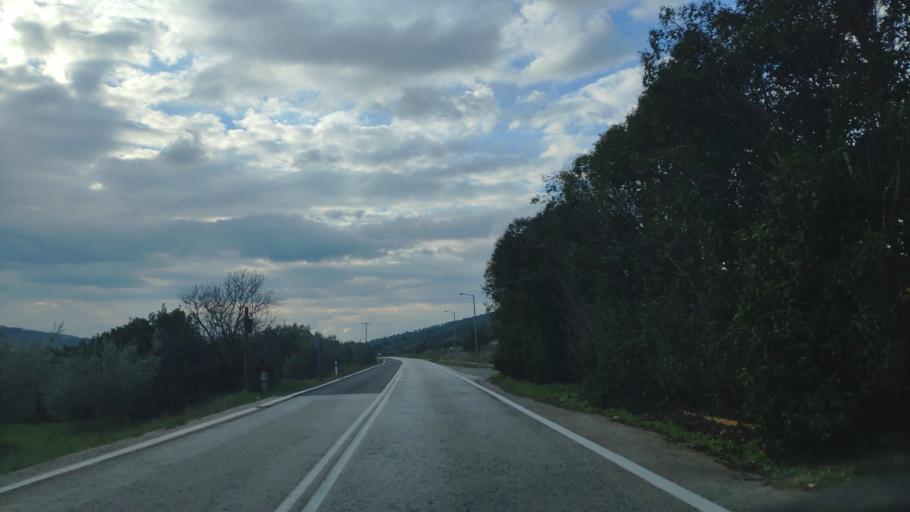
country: GR
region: Peloponnese
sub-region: Nomos Argolidos
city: Koutsopodi
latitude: 37.7504
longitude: 22.7339
